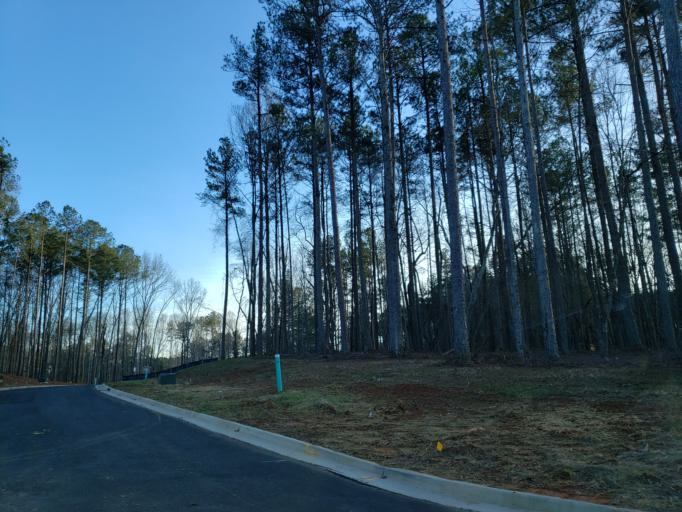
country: US
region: Georgia
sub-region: Cobb County
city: Acworth
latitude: 34.0300
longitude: -84.7315
